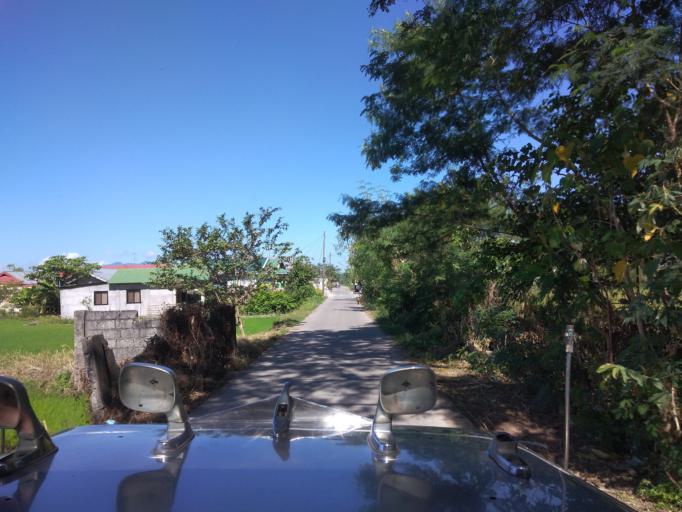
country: PH
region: Central Luzon
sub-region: Province of Pampanga
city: Salapungan
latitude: 15.1533
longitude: 120.9223
